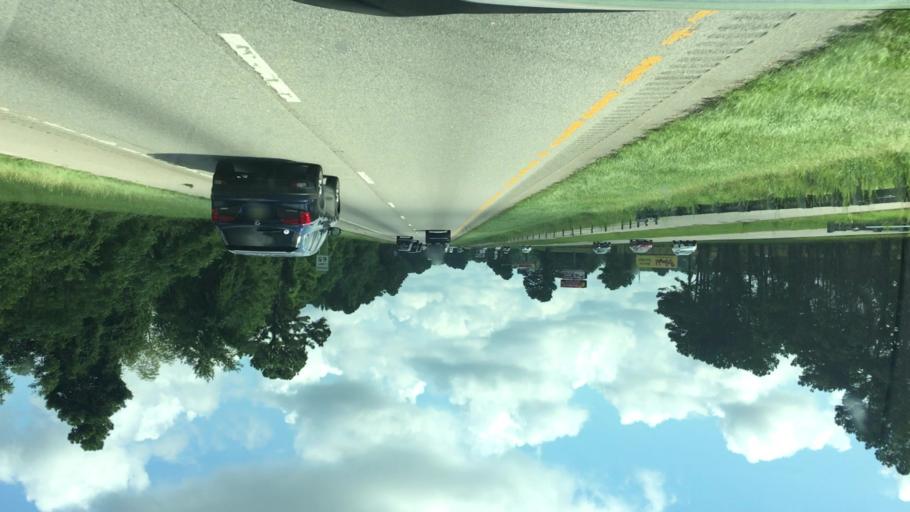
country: US
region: North Carolina
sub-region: Robeson County
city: Lumberton
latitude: 34.7002
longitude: -78.9984
